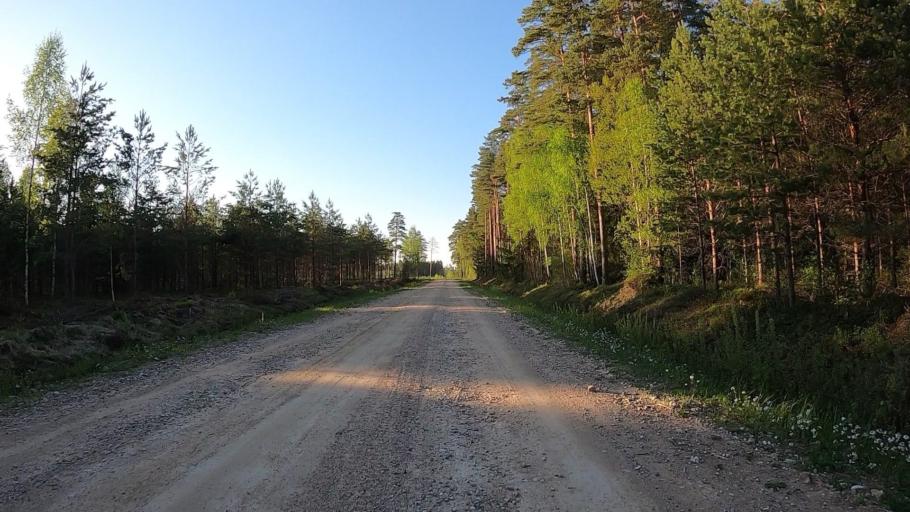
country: LV
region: Kekava
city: Kekava
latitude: 56.7666
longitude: 24.2227
